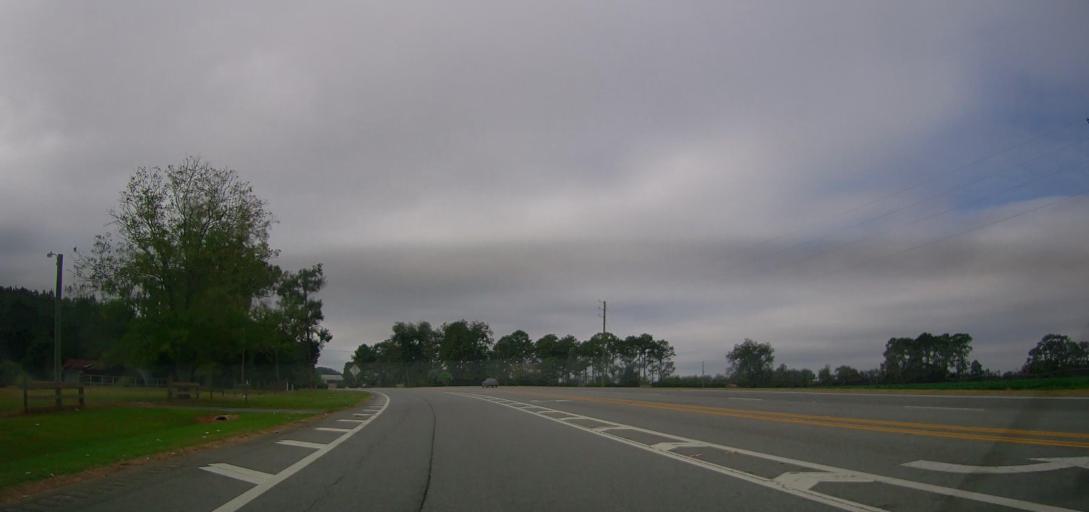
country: US
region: Georgia
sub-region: Tift County
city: Omega
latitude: 31.3337
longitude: -83.6076
